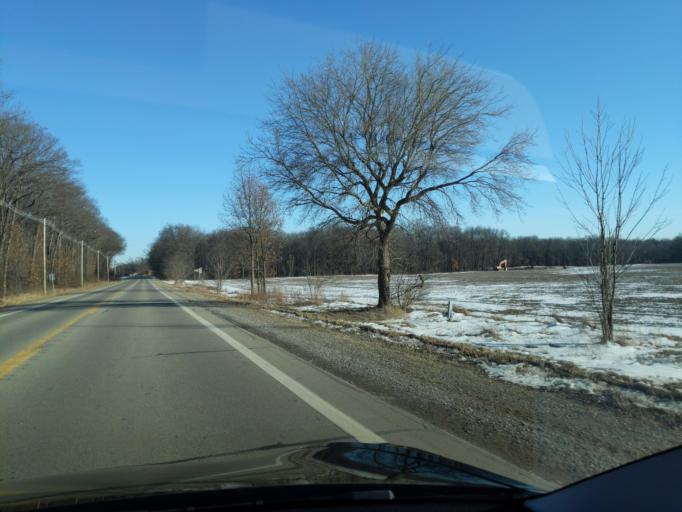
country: US
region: Michigan
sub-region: Ingham County
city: Stockbridge
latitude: 42.3940
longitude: -84.2953
